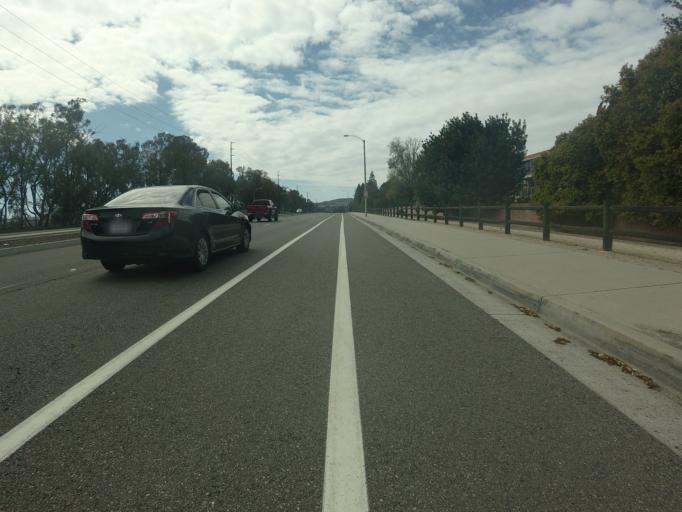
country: US
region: California
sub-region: Orange County
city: Laguna Hills
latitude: 33.5950
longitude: -117.7034
